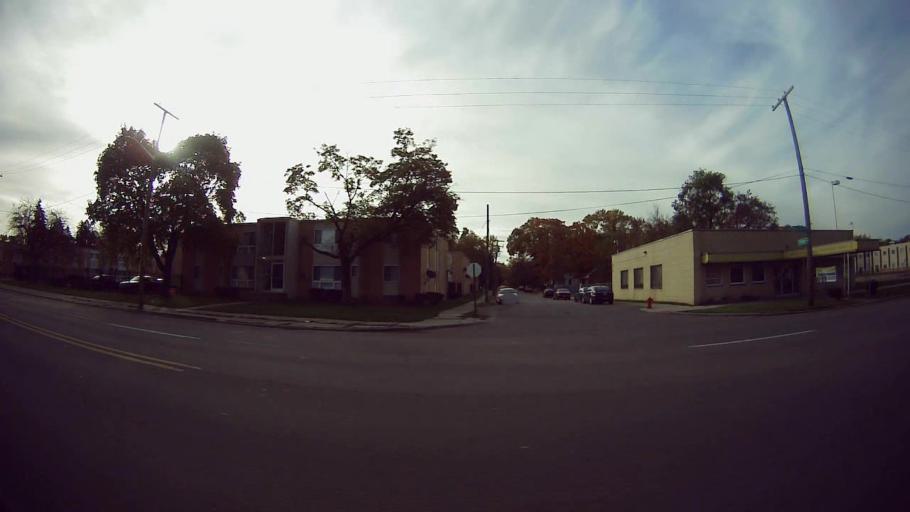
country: US
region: Michigan
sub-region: Oakland County
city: Southfield
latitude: 42.4292
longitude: -83.2548
